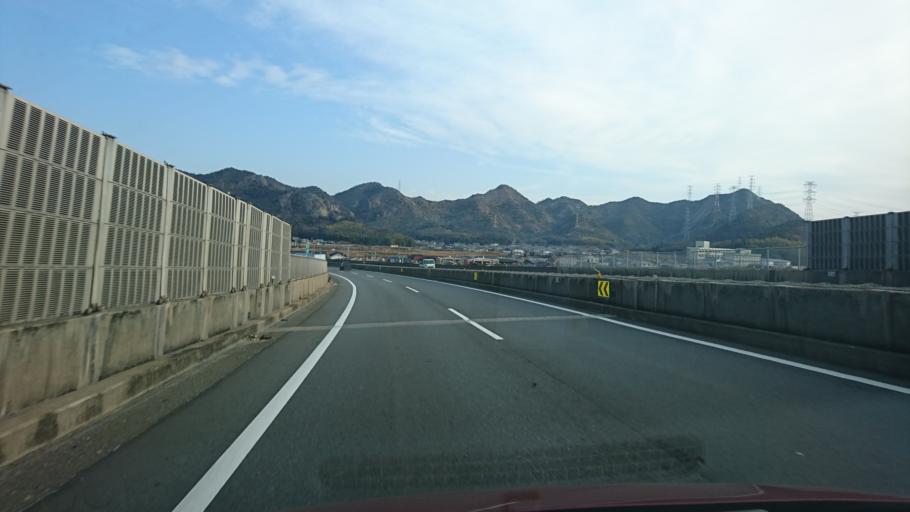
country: JP
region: Hyogo
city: Shirahamacho-usazakiminami
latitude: 34.8129
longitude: 134.7465
